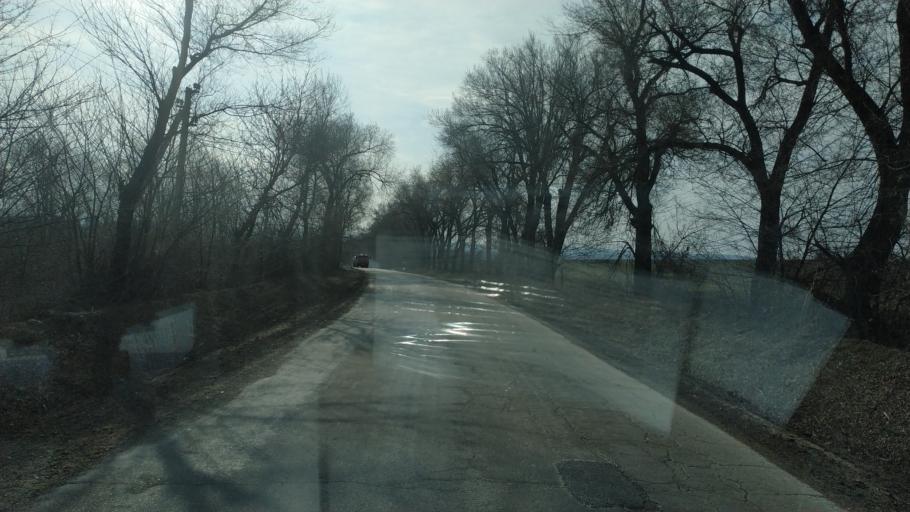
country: MD
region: Chisinau
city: Singera
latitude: 46.9331
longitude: 29.0471
